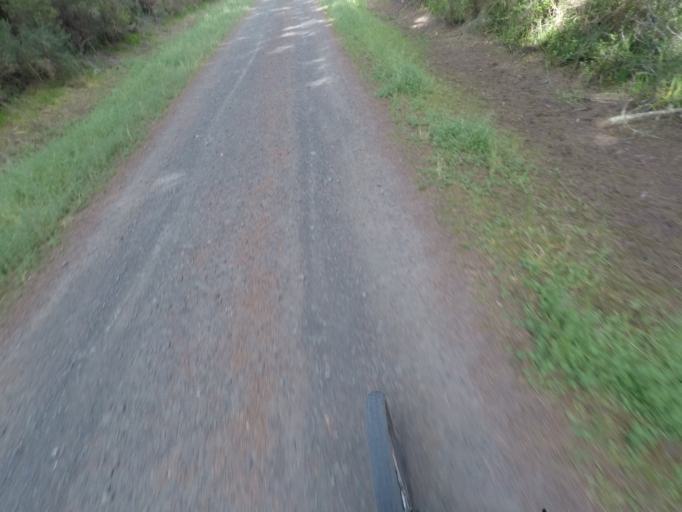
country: NZ
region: Auckland
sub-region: Auckland
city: Muriwai Beach
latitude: -36.7437
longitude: 174.5670
